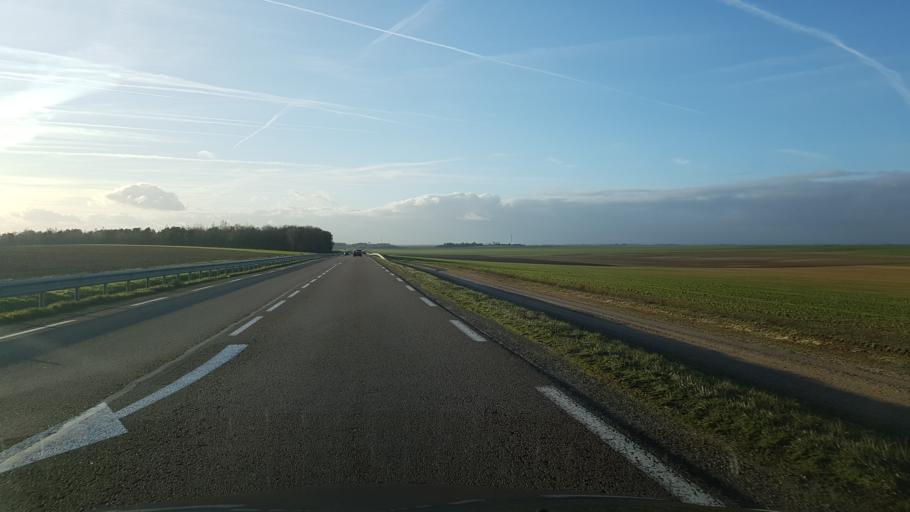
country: FR
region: Champagne-Ardenne
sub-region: Departement de l'Aube
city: Mailly-le-Camp
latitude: 48.7333
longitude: 4.2734
